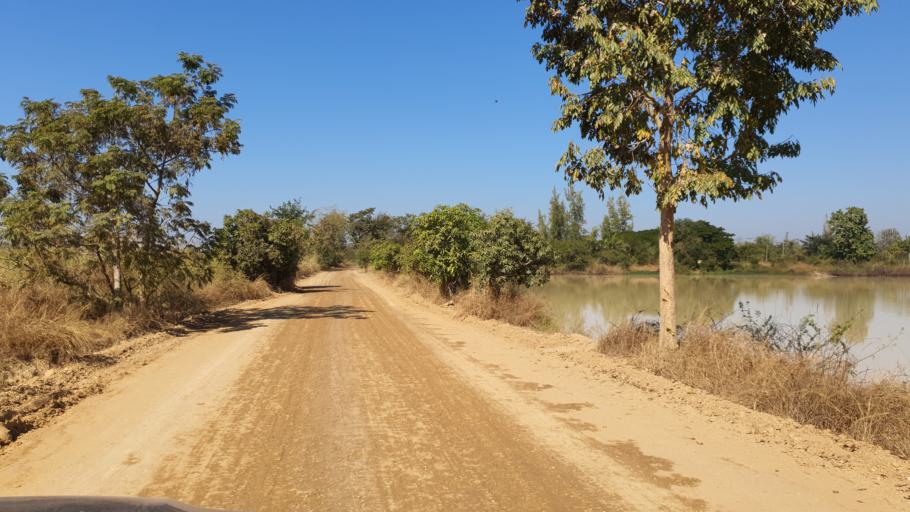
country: TH
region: Lamphun
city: Ban Thi
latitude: 18.6659
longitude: 99.1079
